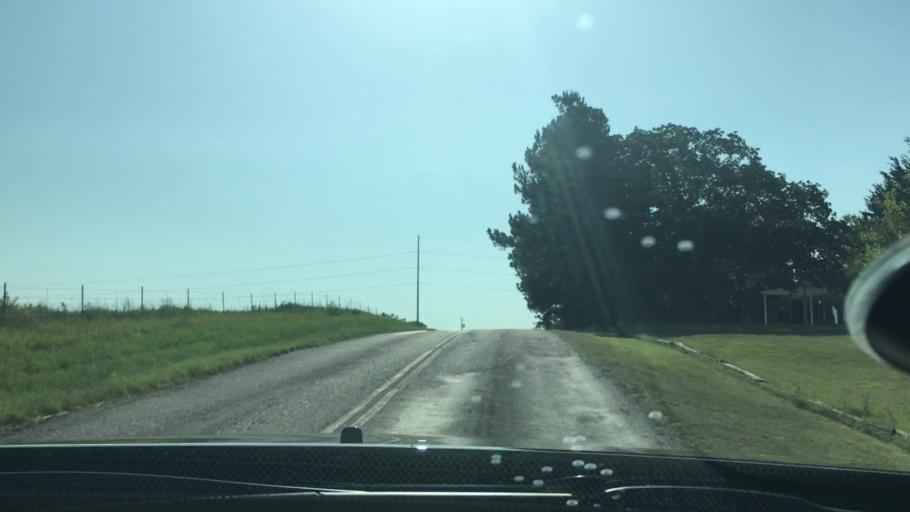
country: US
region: Oklahoma
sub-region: Pontotoc County
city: Ada
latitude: 34.8106
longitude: -96.6370
